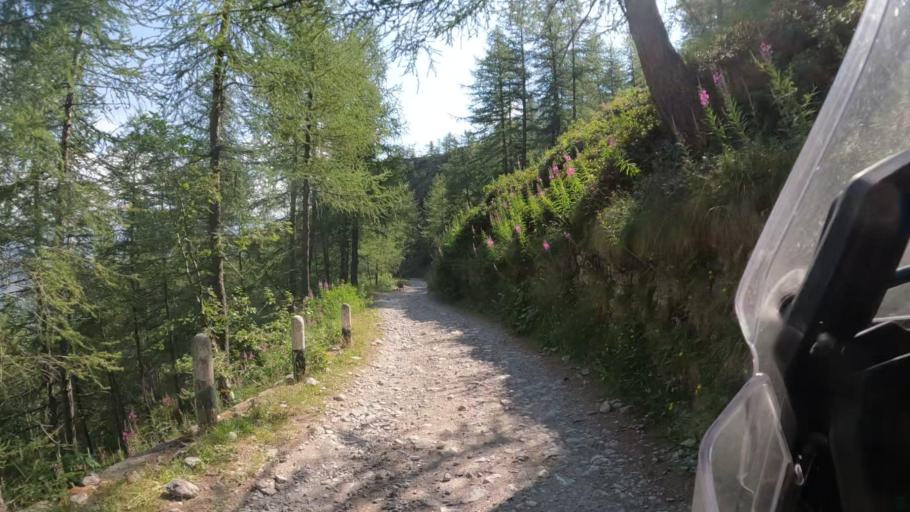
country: IT
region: Piedmont
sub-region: Provincia di Cuneo
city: Briga Alta
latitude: 44.1016
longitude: 7.7155
